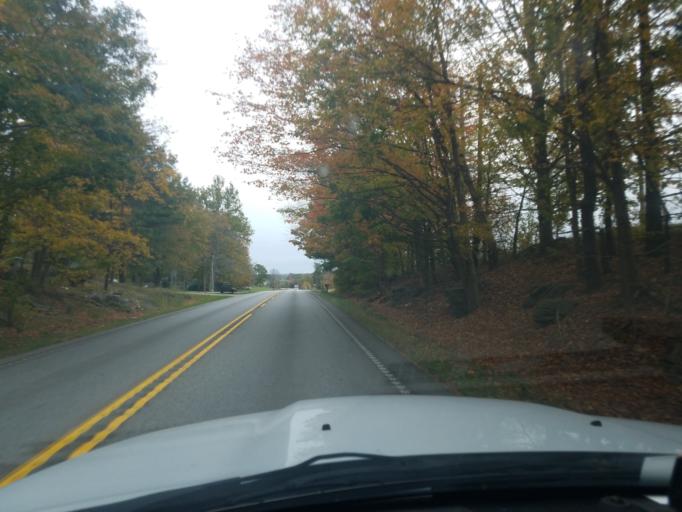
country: US
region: Indiana
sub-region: Washington County
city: New Pekin
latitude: 38.5406
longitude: -86.0341
